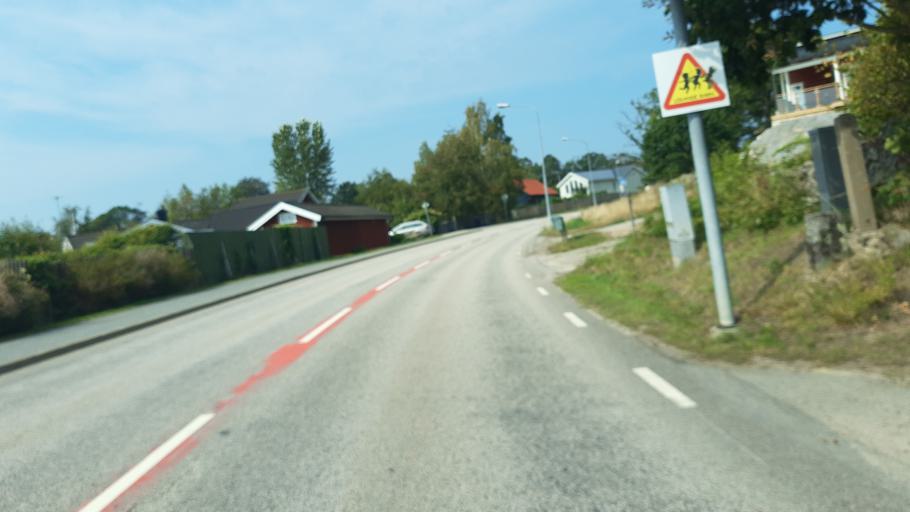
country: SE
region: Blekinge
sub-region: Ronneby Kommun
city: Ronneby
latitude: 56.1733
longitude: 15.2794
